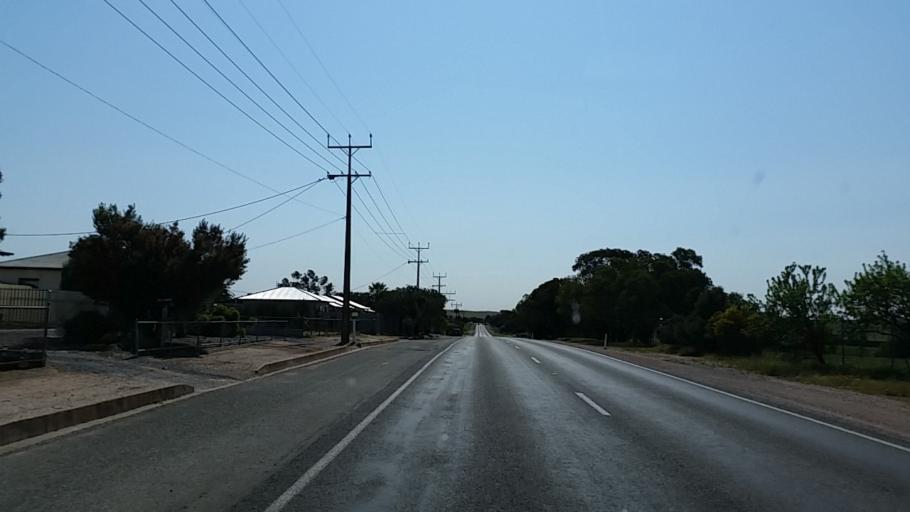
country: AU
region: South Australia
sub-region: Port Pirie City and Dists
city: Crystal Brook
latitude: -33.2599
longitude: 138.3560
